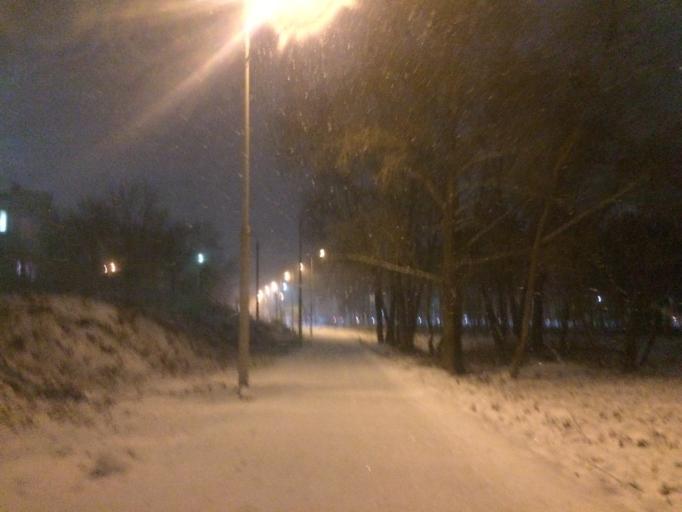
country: RU
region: Tula
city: Tula
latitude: 54.1754
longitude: 37.5898
